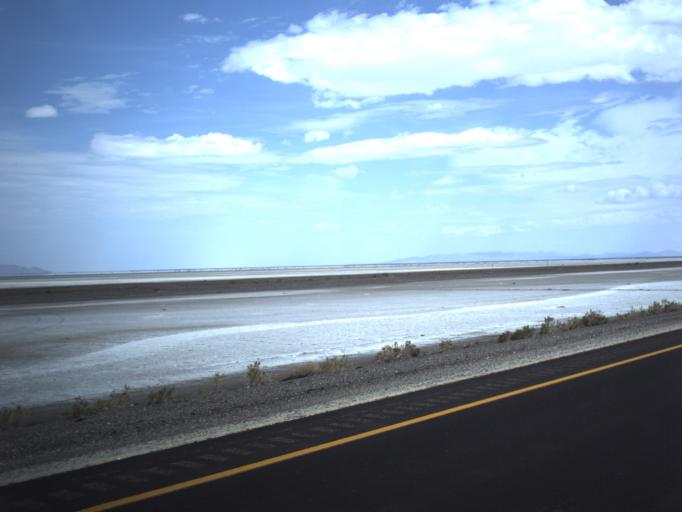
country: US
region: Utah
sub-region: Tooele County
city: Wendover
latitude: 40.7334
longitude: -113.6125
